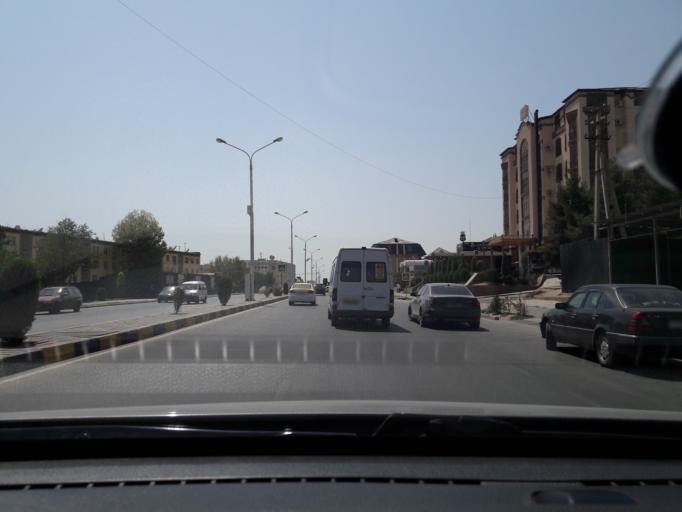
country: TJ
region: Dushanbe
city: Dushanbe
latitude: 38.5912
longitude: 68.7373
